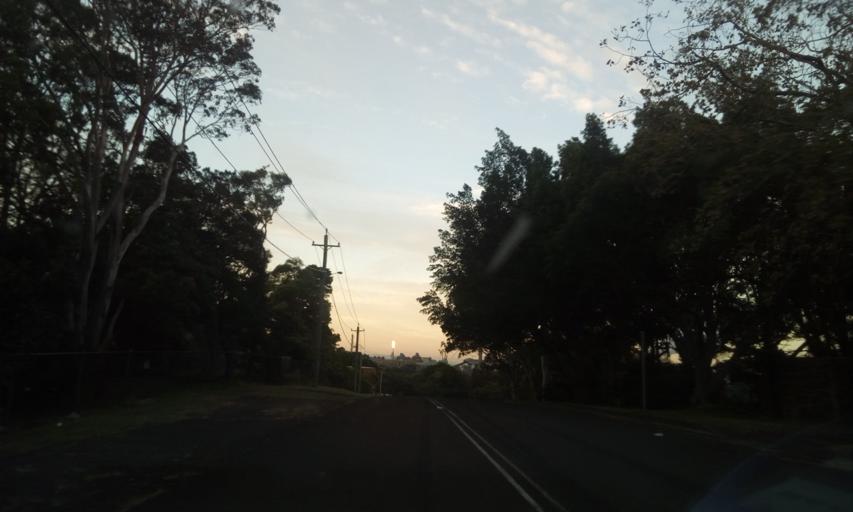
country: AU
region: New South Wales
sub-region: Wollongong
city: Cringila
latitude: -34.4770
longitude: 150.8842
